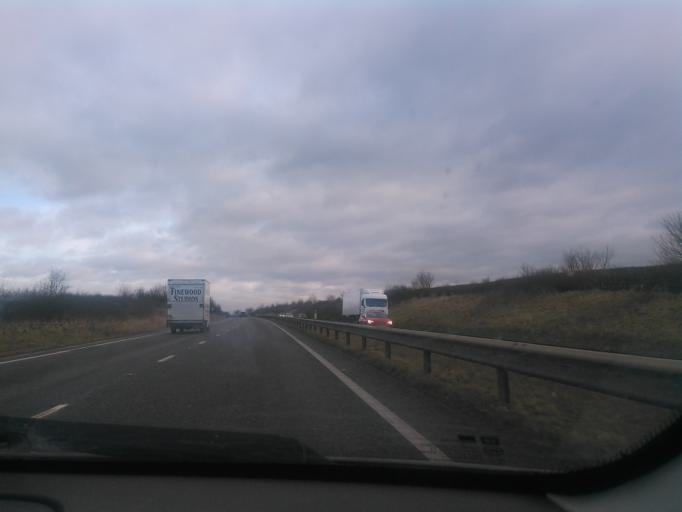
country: GB
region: England
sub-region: Derby
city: Derby
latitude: 52.8637
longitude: -1.4814
